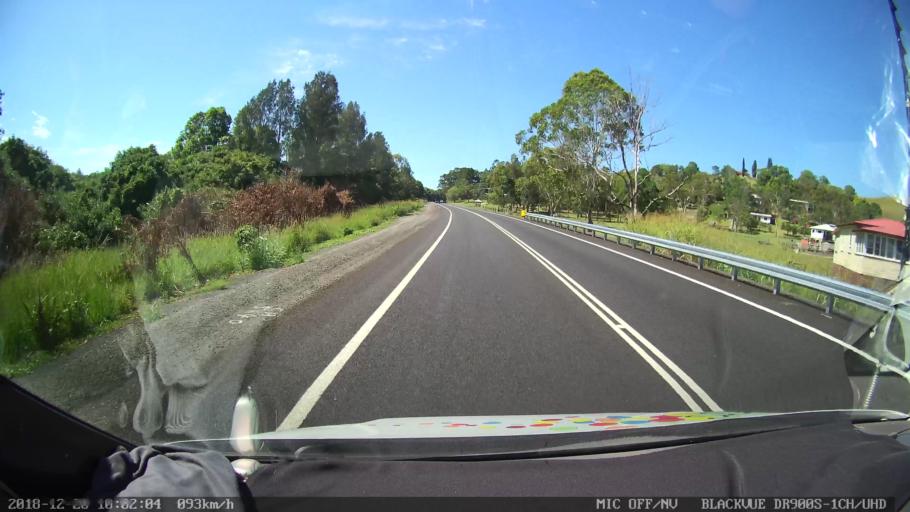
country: AU
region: New South Wales
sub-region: Lismore Municipality
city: Lismore
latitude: -28.8531
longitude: 153.2610
